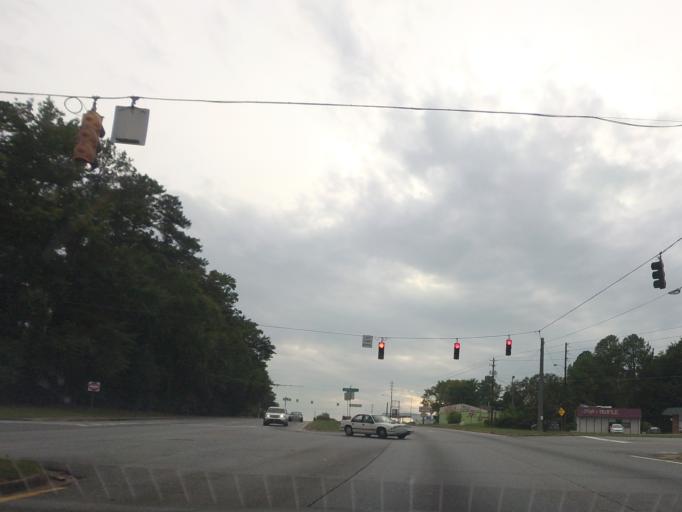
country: US
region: Georgia
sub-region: Bibb County
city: Macon
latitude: 32.8488
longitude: -83.6020
